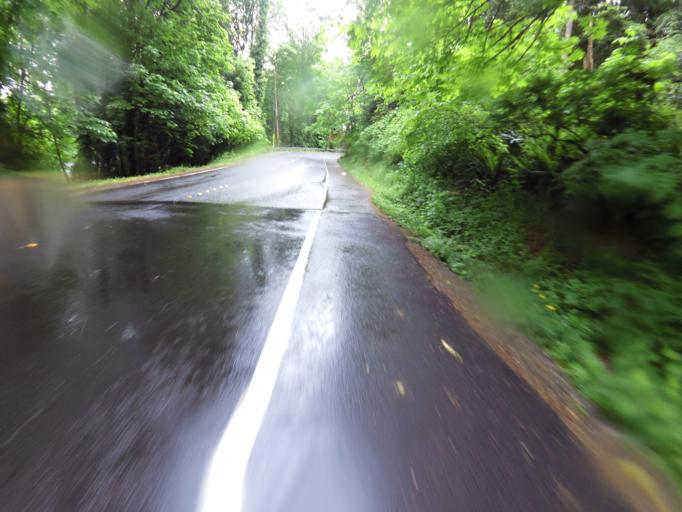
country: US
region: Washington
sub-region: King County
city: Mercer Island
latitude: 47.5557
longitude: -122.2146
